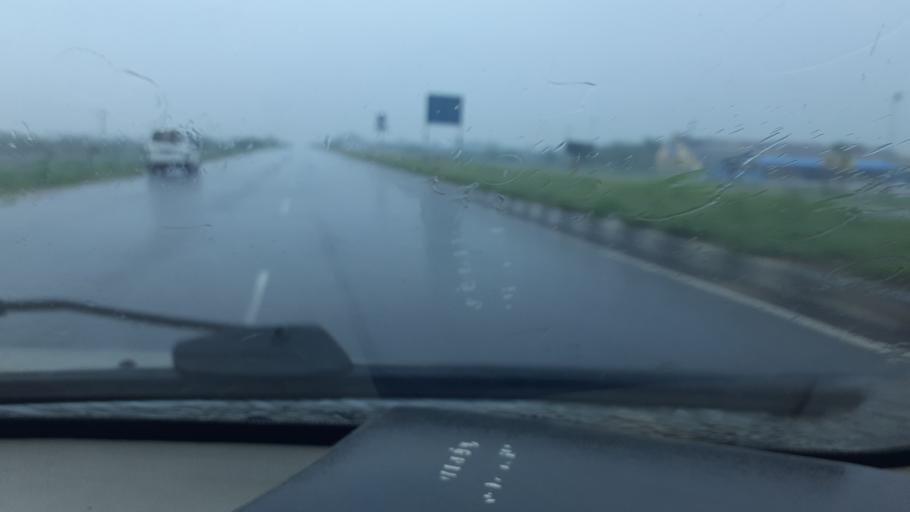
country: IN
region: Tamil Nadu
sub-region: Virudhunagar
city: Sattur
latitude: 9.4332
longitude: 77.9198
